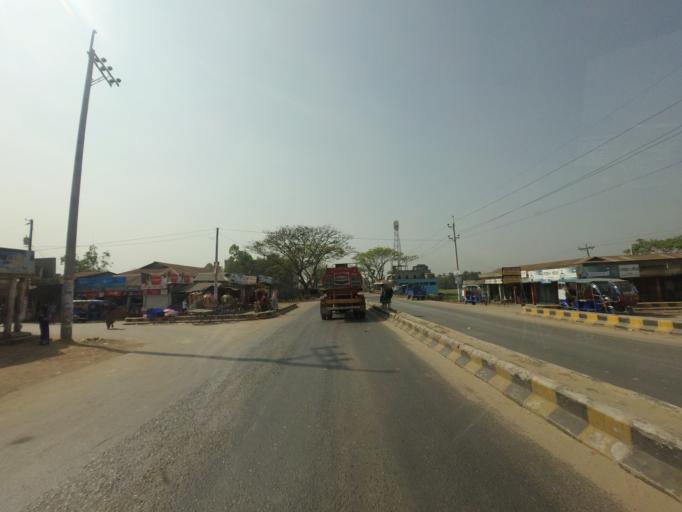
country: BD
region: Sylhet
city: Habiganj
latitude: 24.2984
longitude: 91.5114
